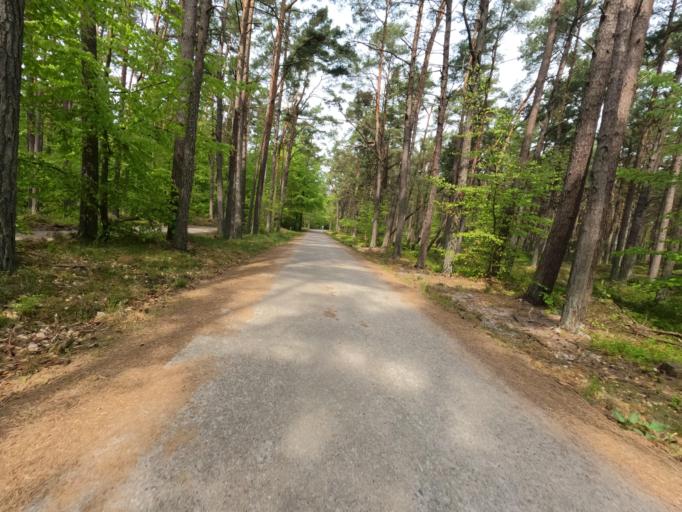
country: DE
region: Mecklenburg-Vorpommern
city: Ostseebad Prerow
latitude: 54.4635
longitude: 12.5145
